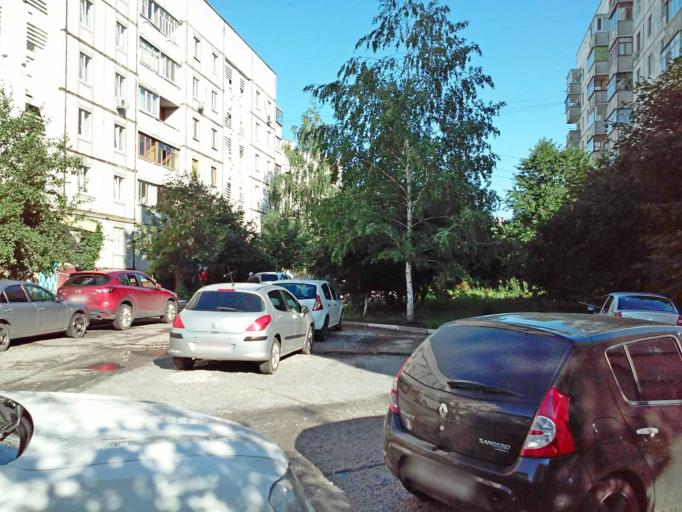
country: RU
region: Belgorod
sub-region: Belgorodskiy Rayon
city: Belgorod
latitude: 50.5556
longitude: 36.5711
